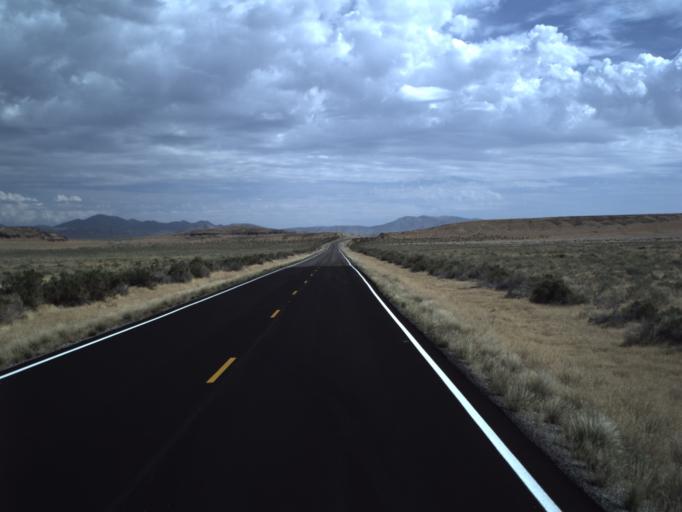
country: US
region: Utah
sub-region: Tooele County
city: Wendover
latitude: 41.4147
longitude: -113.9198
